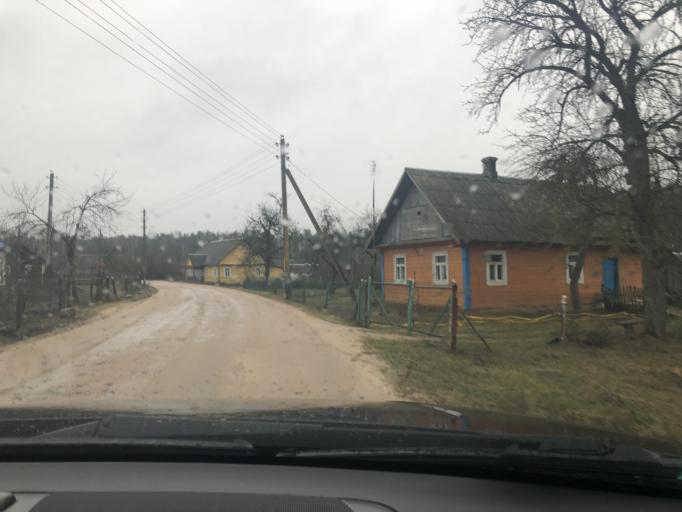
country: BY
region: Grodnenskaya
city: Skidal'
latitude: 53.8580
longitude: 24.2512
